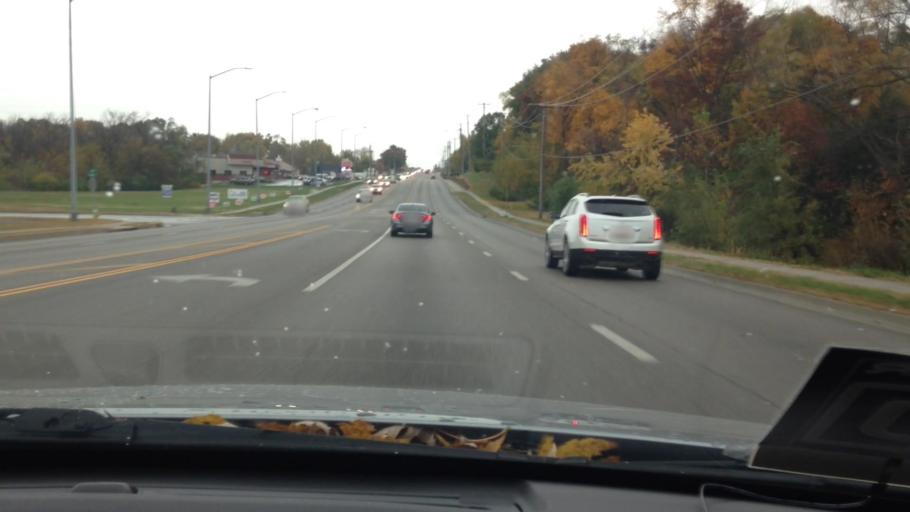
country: US
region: Kansas
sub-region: Leavenworth County
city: Lansing
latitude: 39.2651
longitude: -94.8999
